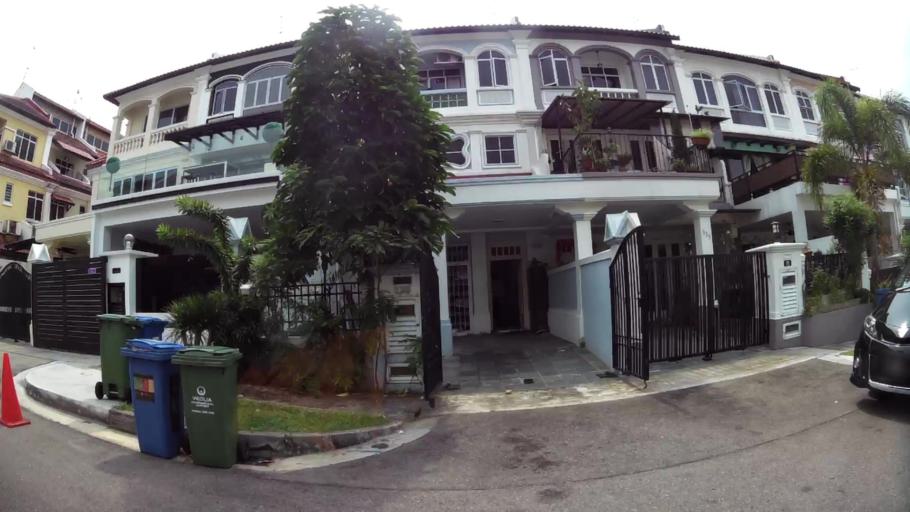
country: SG
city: Singapore
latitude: 1.3648
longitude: 103.9664
